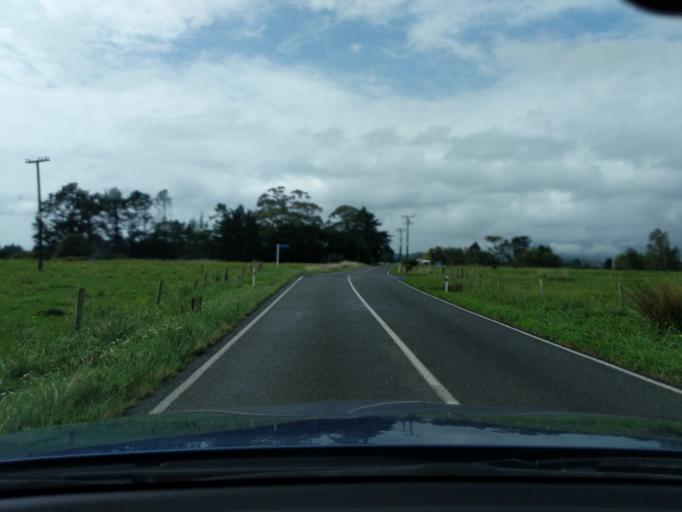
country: NZ
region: Tasman
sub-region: Tasman District
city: Takaka
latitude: -40.6625
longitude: 172.6492
